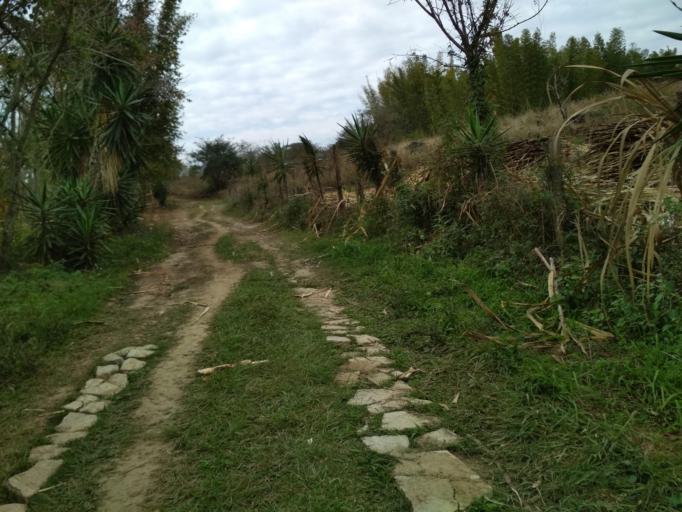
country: MX
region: Veracruz
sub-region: Coatepec
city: Tuzamapan
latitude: 19.3662
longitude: -96.8824
